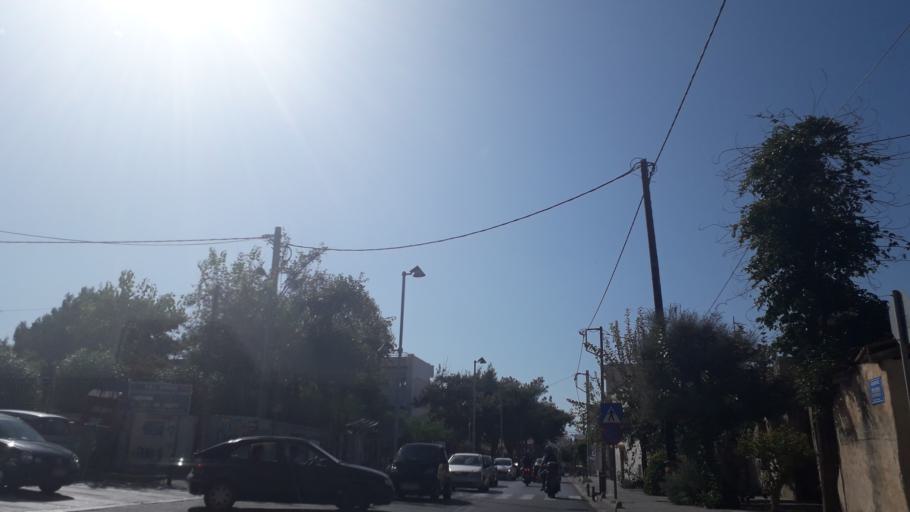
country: GR
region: Crete
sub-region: Nomos Rethymnis
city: Rethymno
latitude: 35.3664
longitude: 24.5019
